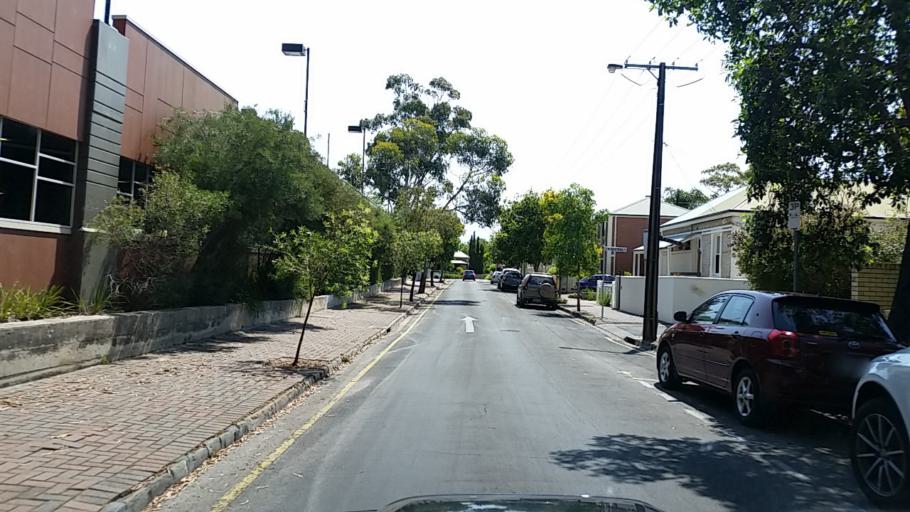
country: AU
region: South Australia
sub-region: Norwood Payneham St Peters
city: Trinity Gardens
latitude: -34.9196
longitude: 138.6356
